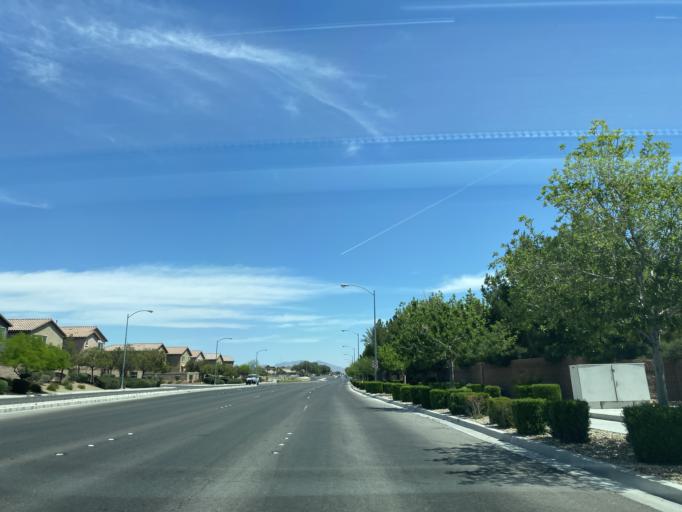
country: US
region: Nevada
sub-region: Clark County
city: Nellis Air Force Base
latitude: 36.2691
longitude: -115.0943
